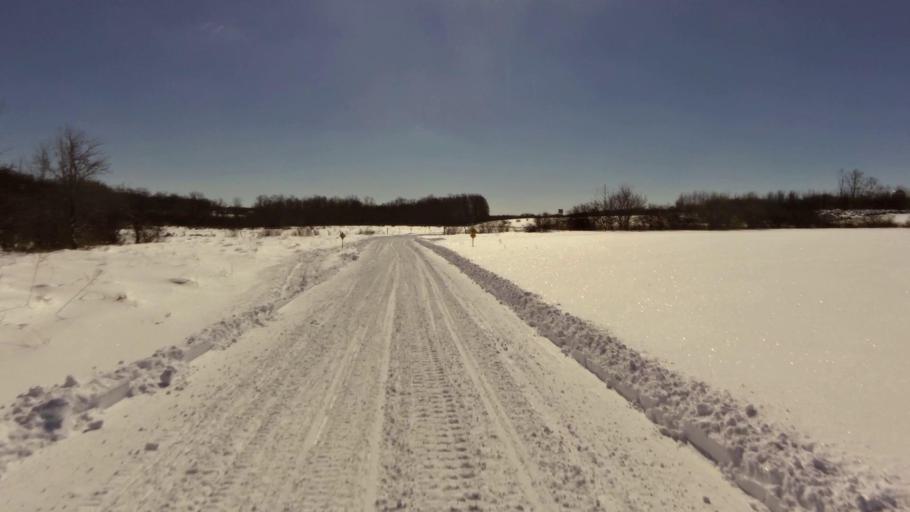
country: US
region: New York
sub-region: Chautauqua County
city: Mayville
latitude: 42.2240
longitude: -79.3943
